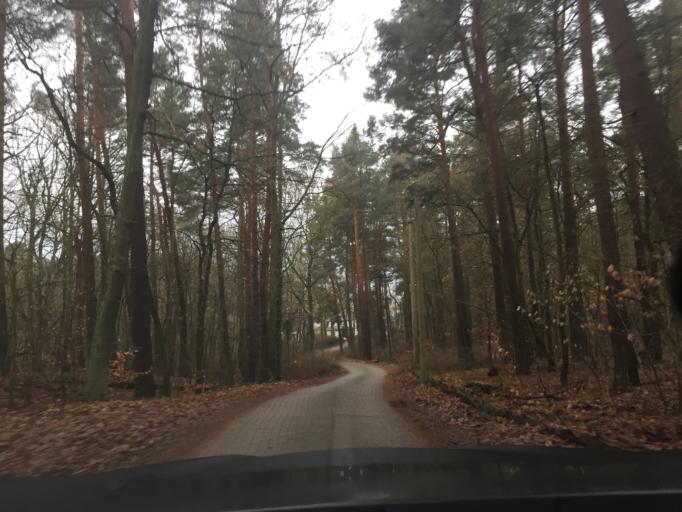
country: DE
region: Berlin
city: Kladow
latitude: 52.4541
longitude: 13.1076
